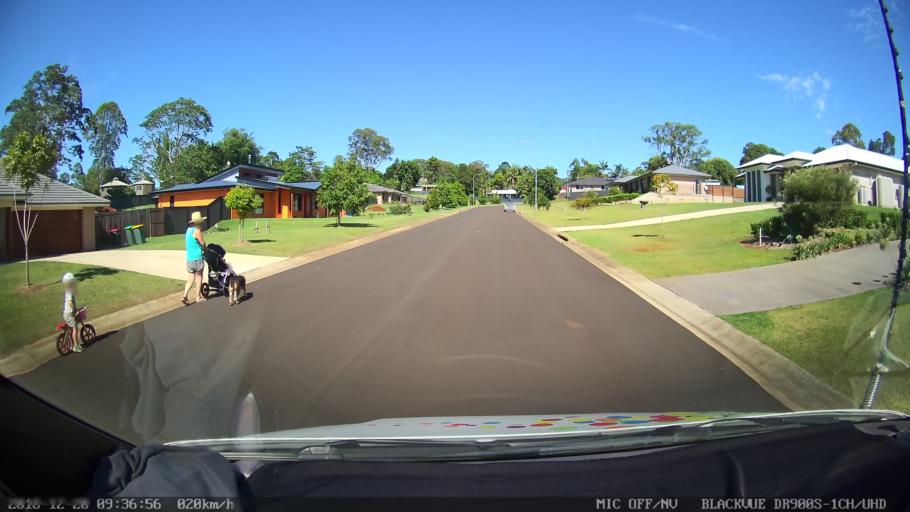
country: AU
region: New South Wales
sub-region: Lismore Municipality
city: Nimbin
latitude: -28.6858
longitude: 153.3186
